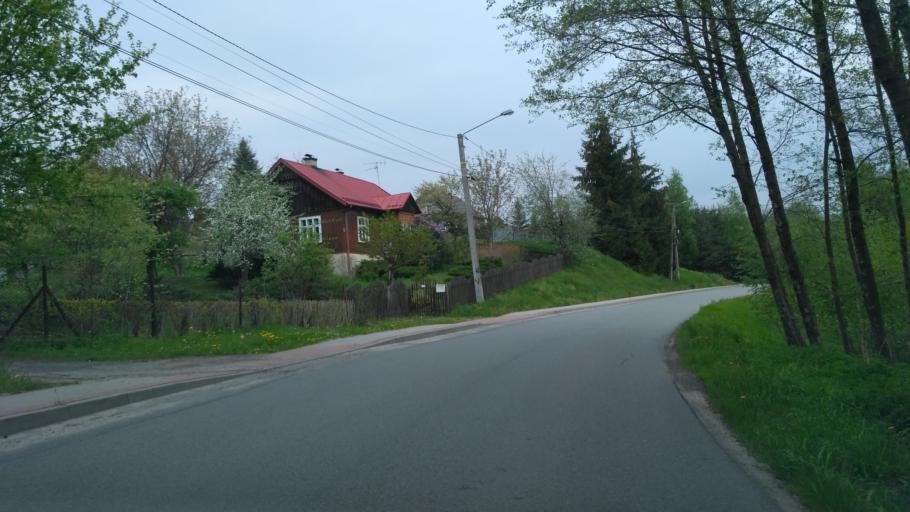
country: PL
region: Lesser Poland Voivodeship
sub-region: Powiat tarnowski
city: Skrzyszow
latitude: 49.9638
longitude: 21.0457
